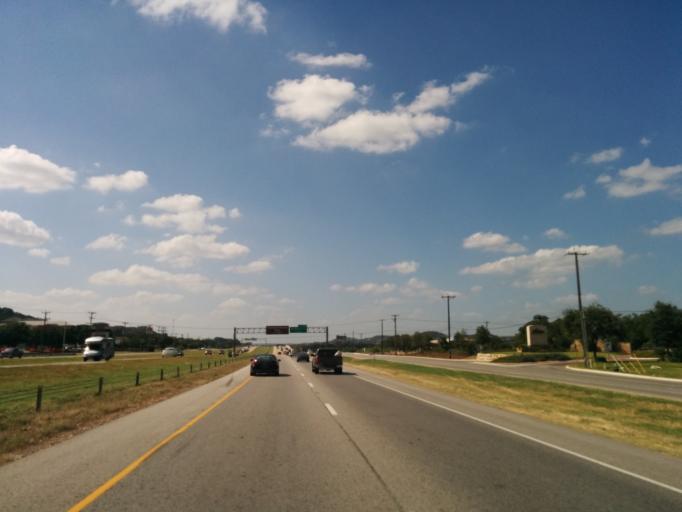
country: US
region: Texas
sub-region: Bexar County
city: Cross Mountain
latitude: 29.6180
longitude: -98.6073
